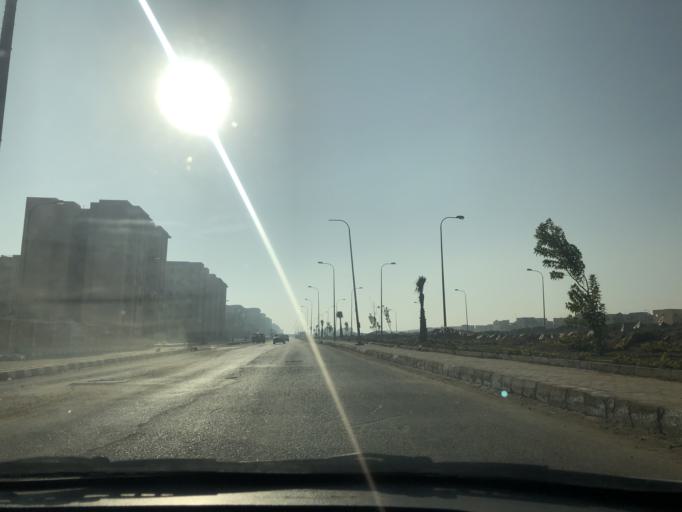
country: EG
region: Al Jizah
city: Madinat Sittah Uktubar
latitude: 29.9260
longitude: 31.0330
